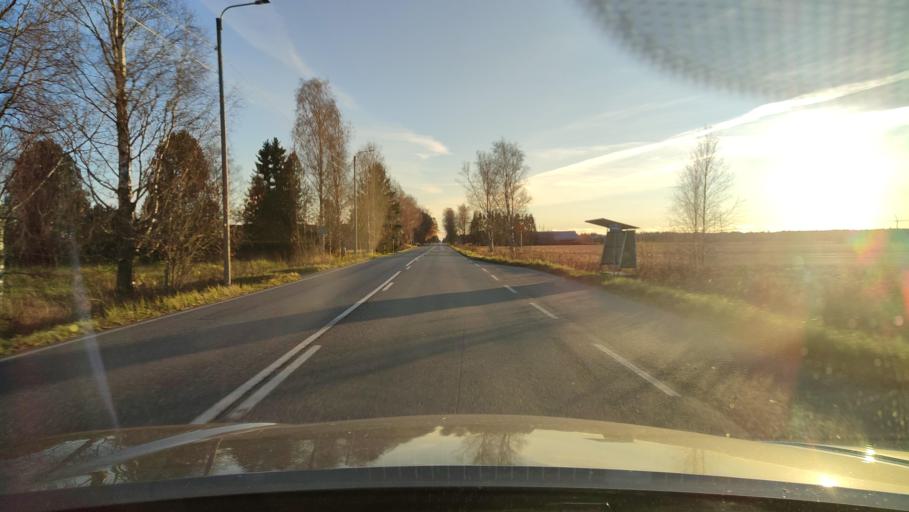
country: FI
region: Ostrobothnia
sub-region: Sydosterbotten
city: Naerpes
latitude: 62.5946
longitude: 21.4486
